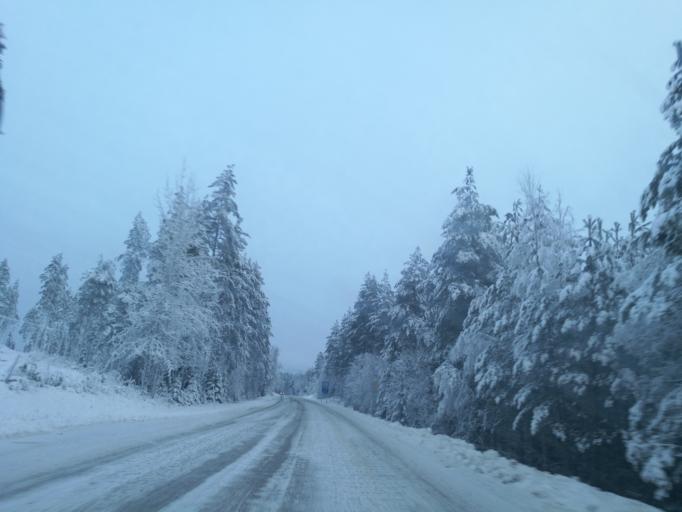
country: NO
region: Hedmark
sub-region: Grue
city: Kirkenaer
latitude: 60.4099
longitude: 12.3908
